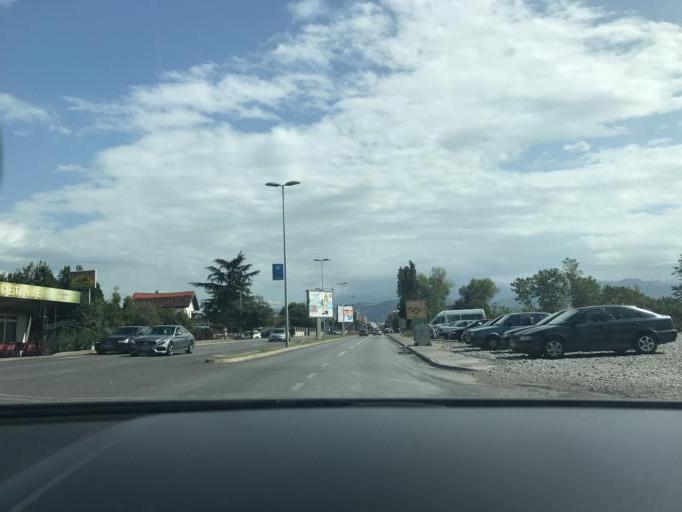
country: ME
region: Podgorica
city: Podgorica
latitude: 42.4343
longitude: 19.2259
